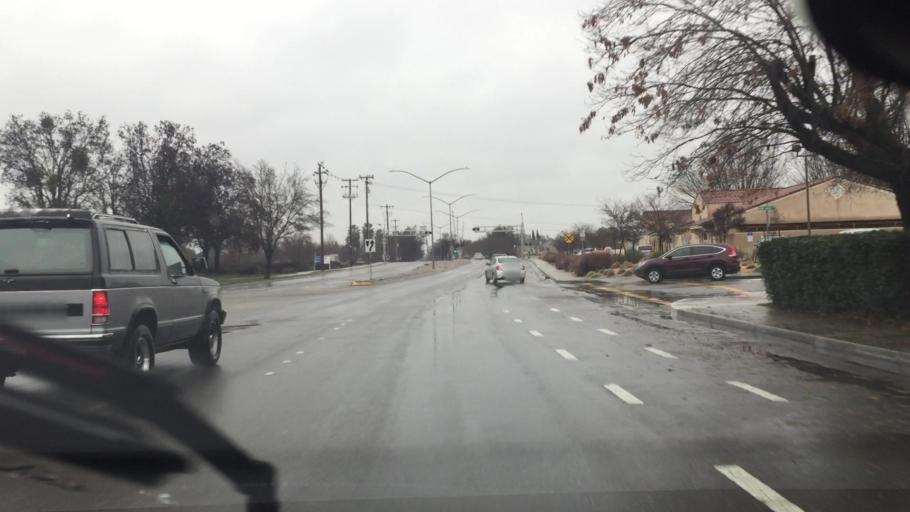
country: US
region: California
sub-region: San Joaquin County
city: Tracy
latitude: 37.7286
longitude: -121.4348
